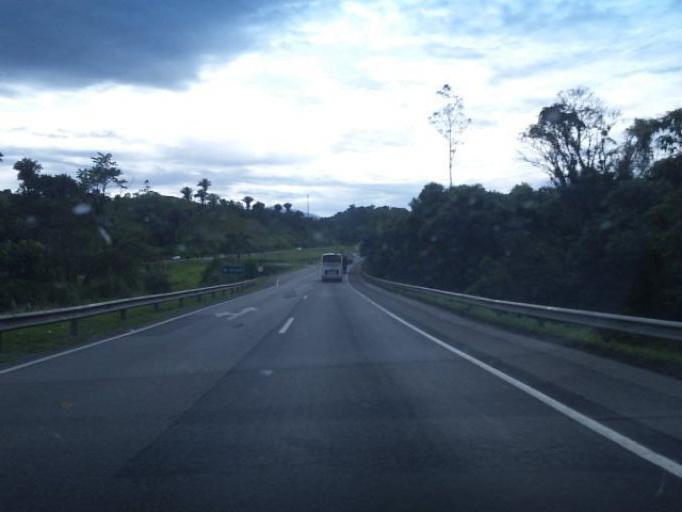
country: BR
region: Parana
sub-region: Antonina
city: Antonina
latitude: -25.0966
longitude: -48.6653
